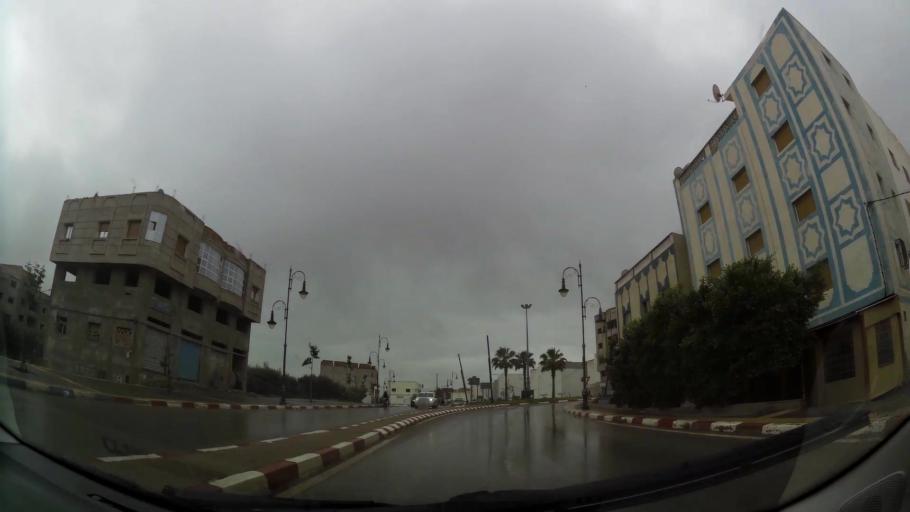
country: MA
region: Taza-Al Hoceima-Taounate
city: Imzourene
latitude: 35.1438
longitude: -3.8480
